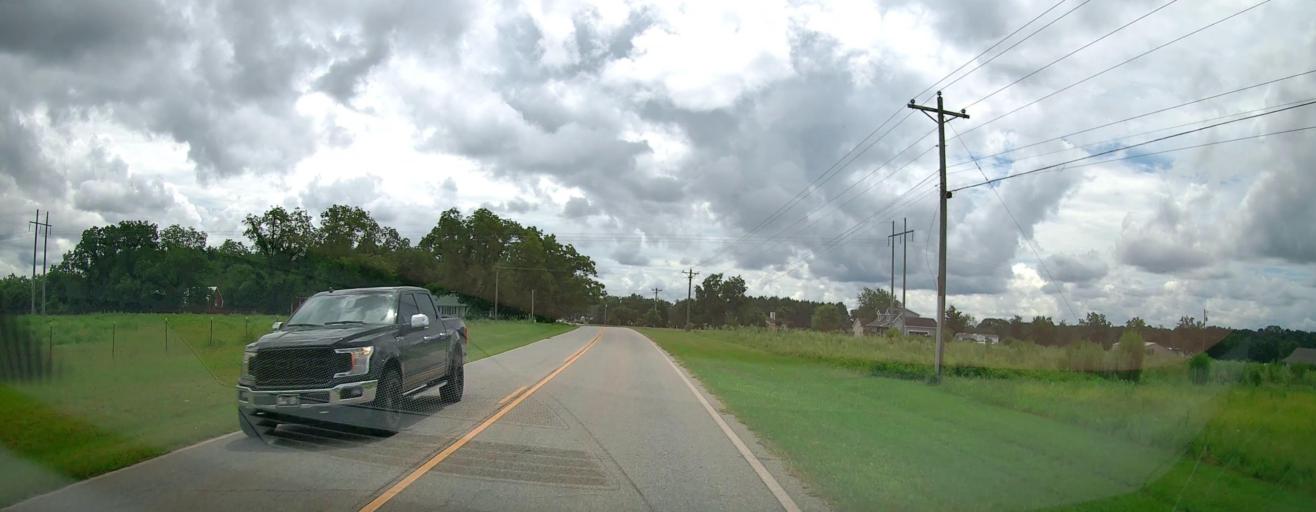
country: US
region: Georgia
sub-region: Peach County
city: Byron
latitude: 32.5641
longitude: -83.7533
